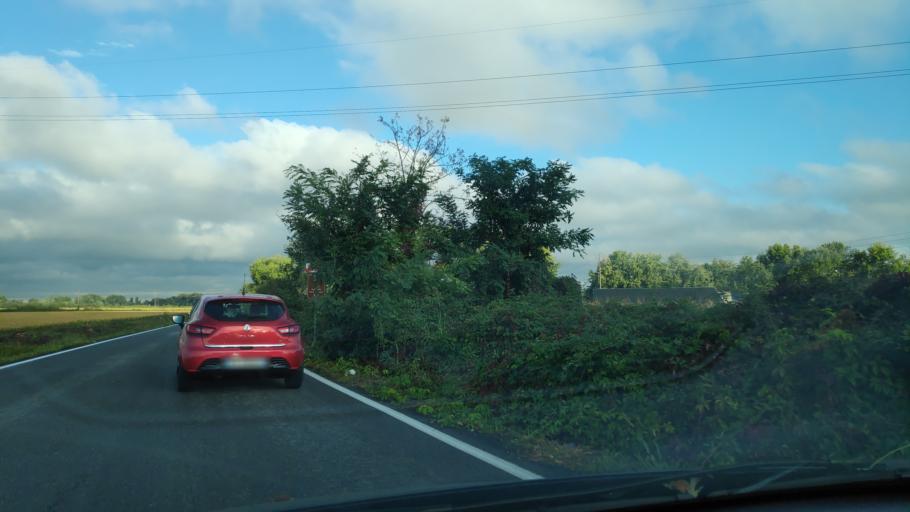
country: IT
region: Lombardy
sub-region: Citta metropolitana di Milano
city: Opera
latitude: 45.3827
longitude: 9.2069
